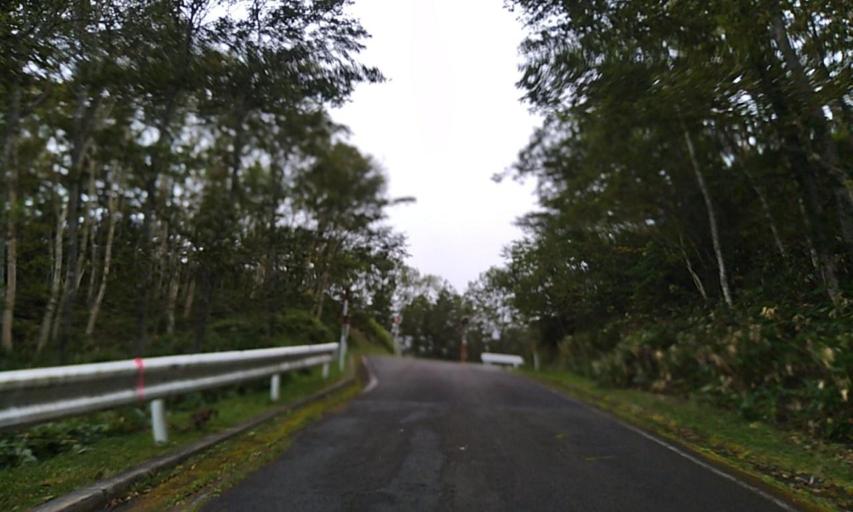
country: JP
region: Hokkaido
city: Bihoro
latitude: 43.5775
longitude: 144.2370
